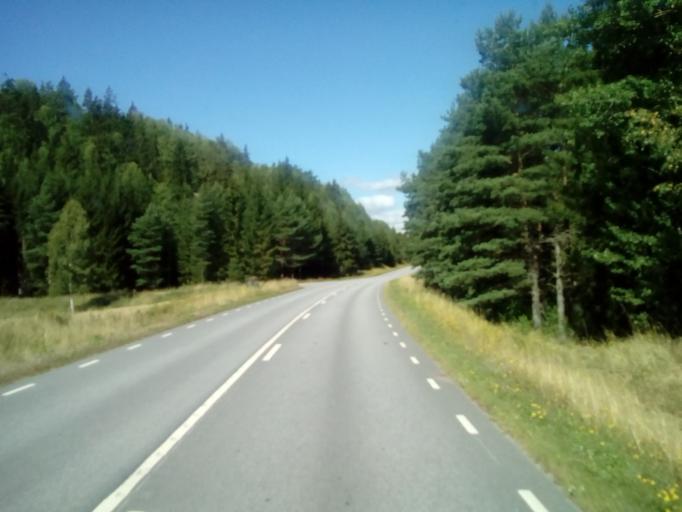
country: SE
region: Kalmar
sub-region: Vimmerby Kommun
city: Sodra Vi
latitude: 57.9151
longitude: 15.9534
